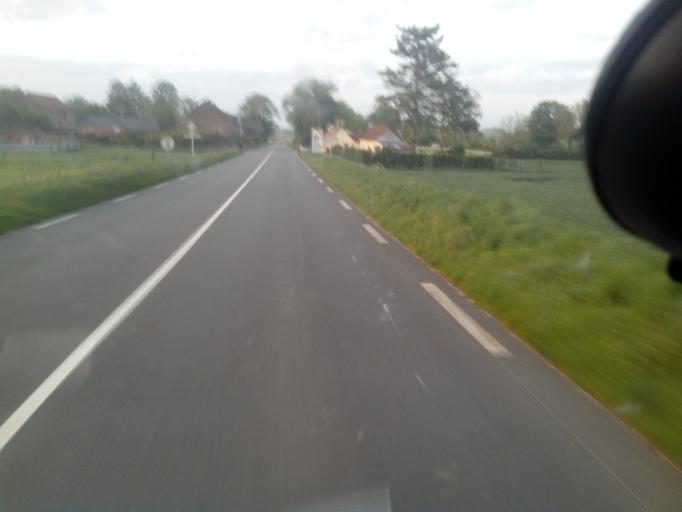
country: FR
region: Picardie
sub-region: Departement de la Somme
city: Crecy-en-Ponthieu
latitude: 50.2245
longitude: 1.9272
